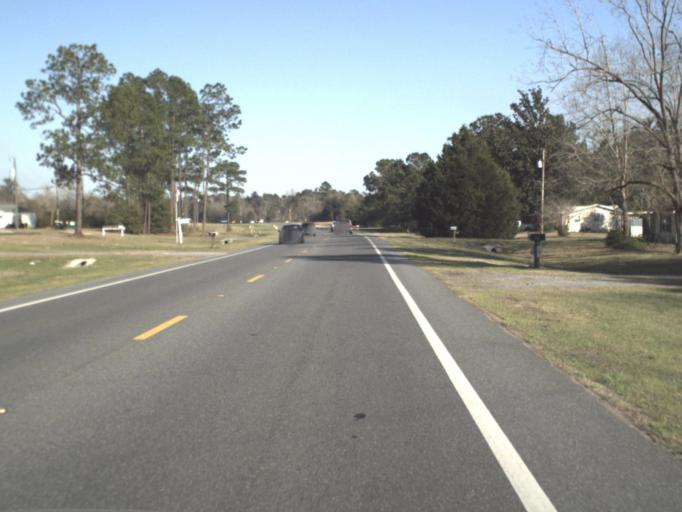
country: US
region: Florida
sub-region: Jackson County
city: Marianna
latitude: 30.7406
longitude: -85.1460
